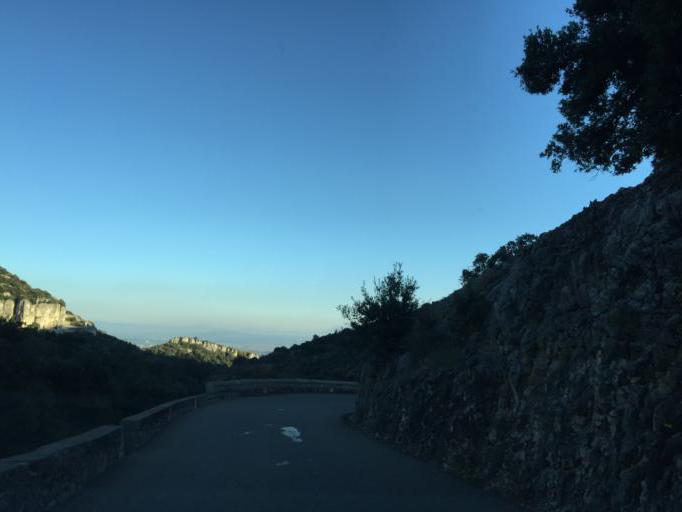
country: FR
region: Rhone-Alpes
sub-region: Departement de l'Ardeche
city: Bourg-Saint-Andeol
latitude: 44.4455
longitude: 4.6107
